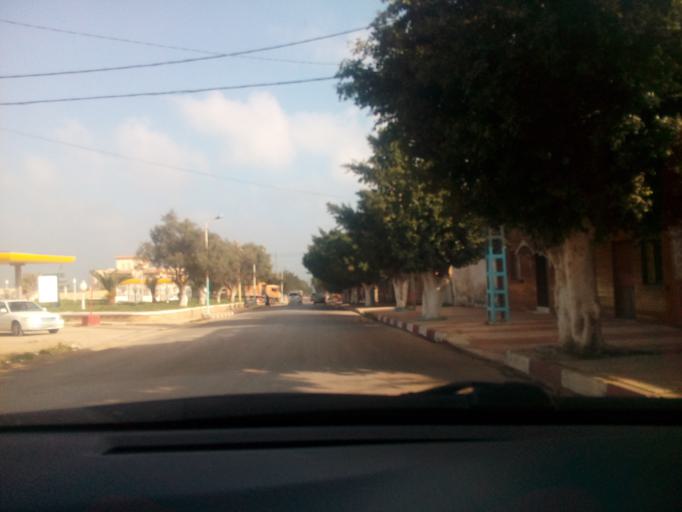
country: DZ
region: Oran
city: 'Ain el Turk
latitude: 35.7033
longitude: -0.8090
